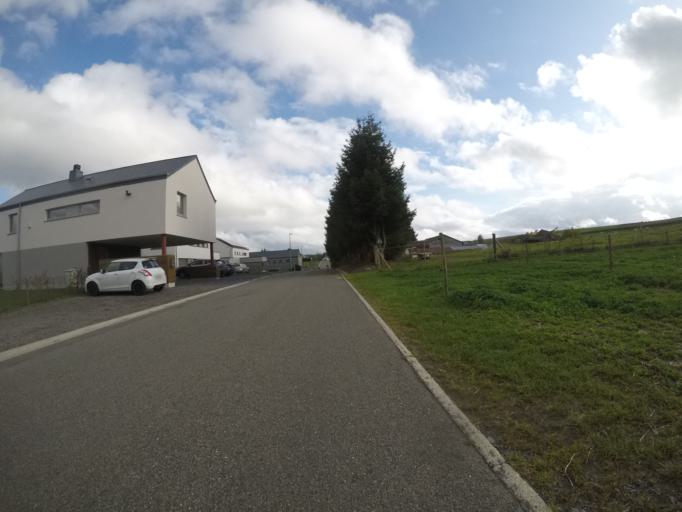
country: BE
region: Wallonia
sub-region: Province du Luxembourg
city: Bastogne
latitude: 49.9565
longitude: 5.6894
